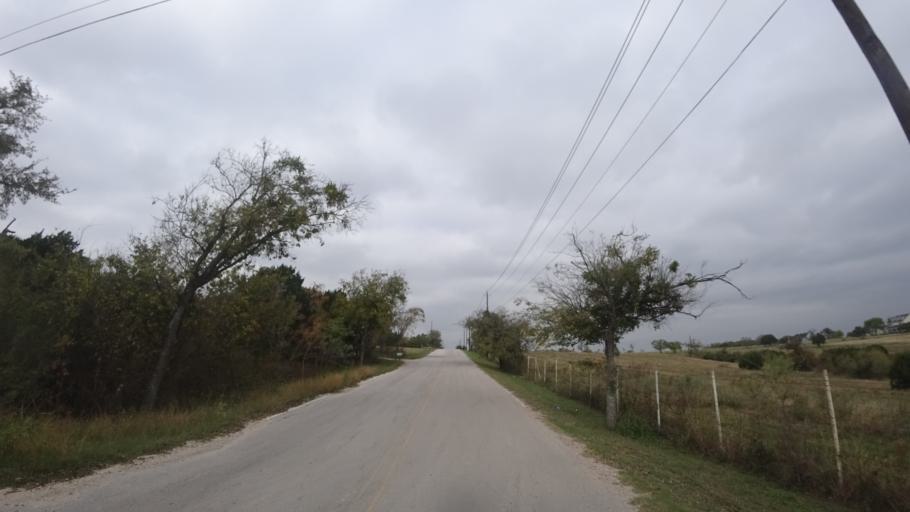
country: US
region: Texas
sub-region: Travis County
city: Pflugerville
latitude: 30.3834
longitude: -97.6101
